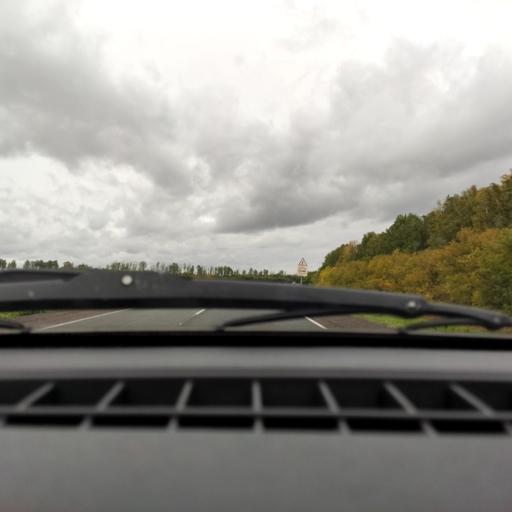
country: RU
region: Bashkortostan
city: Chishmy
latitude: 54.4927
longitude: 55.2763
